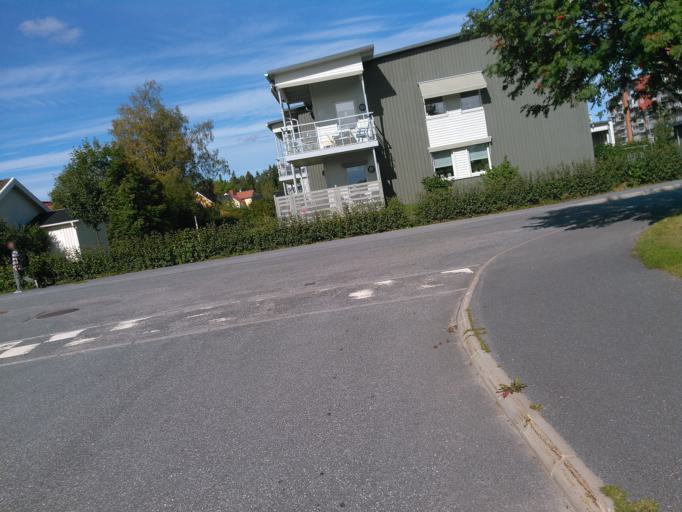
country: SE
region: Vaesterbotten
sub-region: Umea Kommun
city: Umea
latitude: 63.7980
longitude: 20.3121
